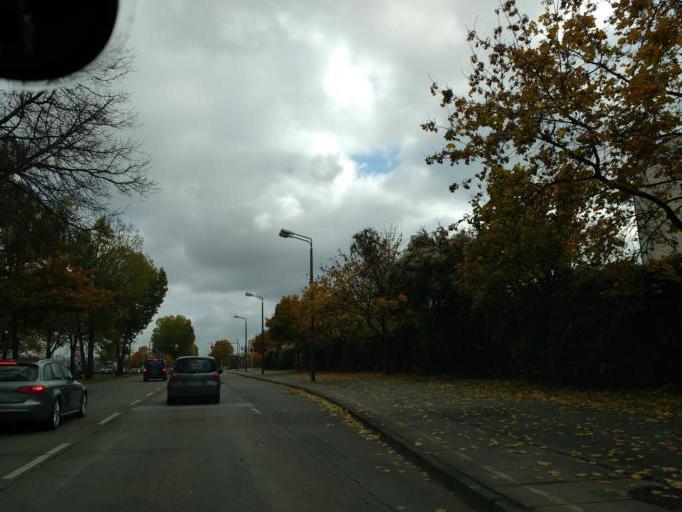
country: DE
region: Berlin
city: Marzahn
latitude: 52.5487
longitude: 13.5912
